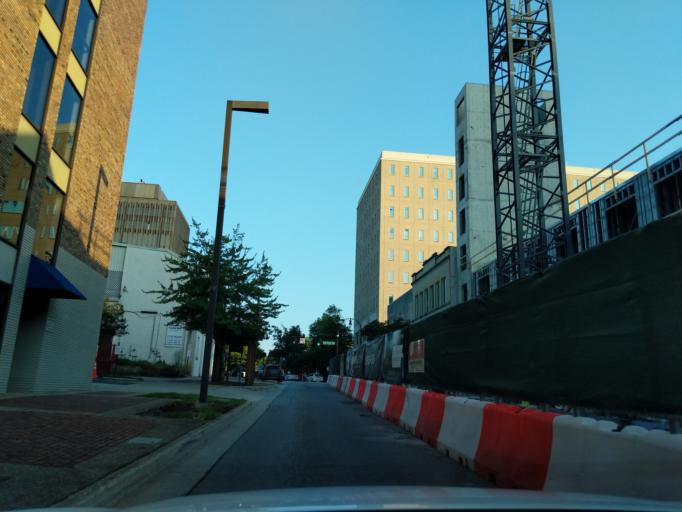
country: US
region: Alabama
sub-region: Madison County
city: Huntsville
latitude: 34.7310
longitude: -86.5864
